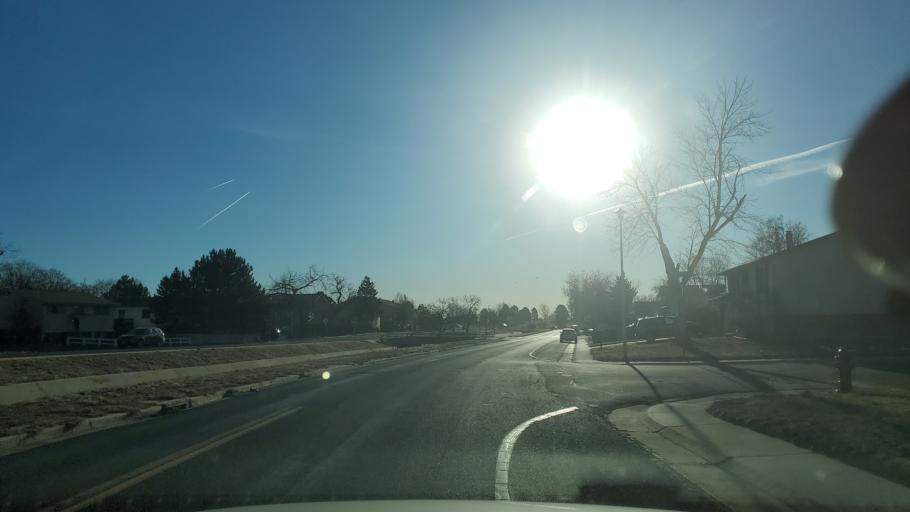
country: US
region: Colorado
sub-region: Adams County
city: Welby
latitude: 39.8438
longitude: -104.9698
